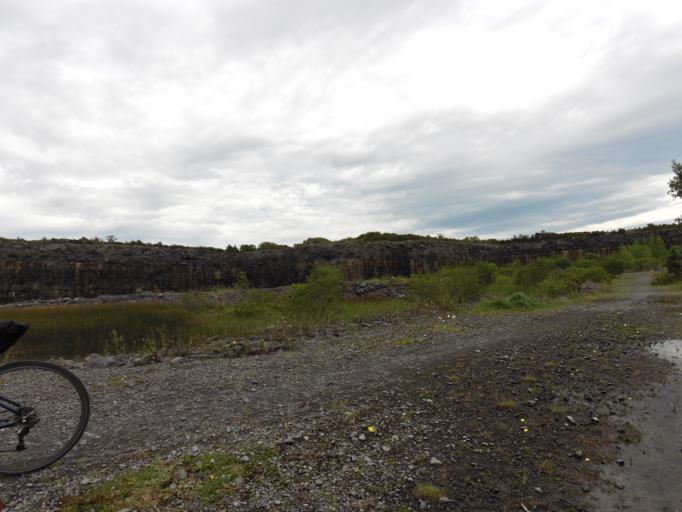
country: IE
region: Connaught
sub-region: County Galway
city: Gaillimh
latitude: 53.3157
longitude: -9.0616
